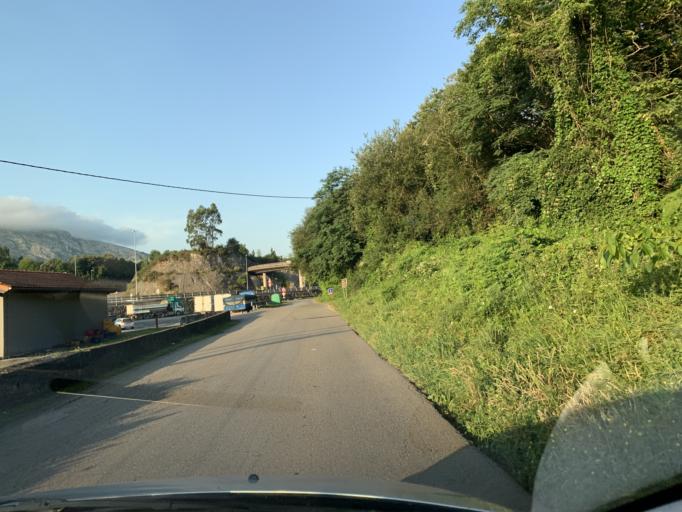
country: ES
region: Asturias
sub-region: Province of Asturias
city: Llanes
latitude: 43.4333
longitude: -4.8582
